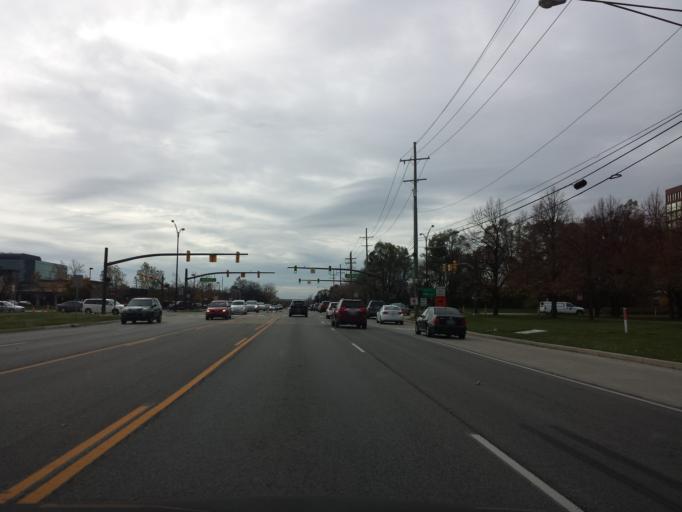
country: US
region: Michigan
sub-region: Oakland County
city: Clawson
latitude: 42.5633
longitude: -83.1478
